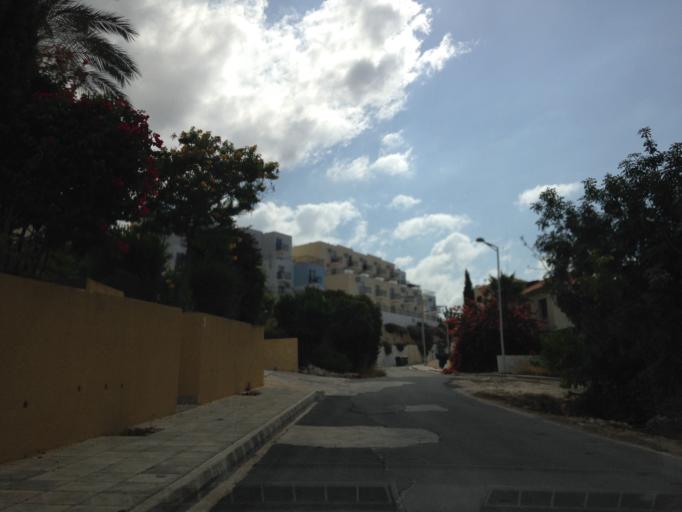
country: CY
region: Pafos
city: Pegeia
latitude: 34.8878
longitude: 32.3865
